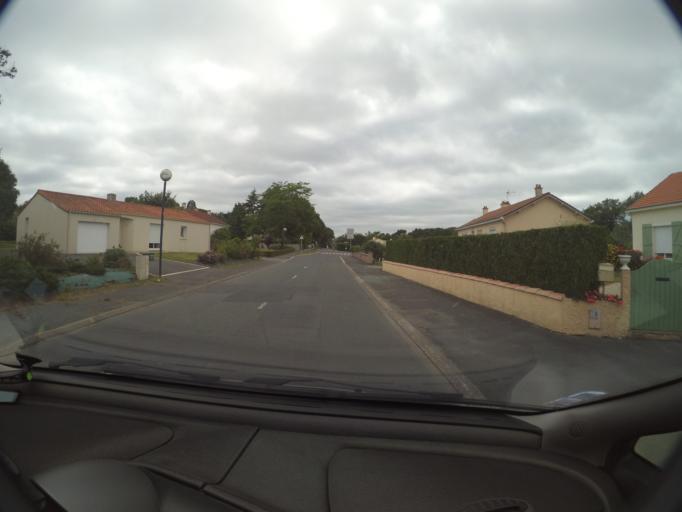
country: FR
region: Pays de la Loire
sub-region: Departement de la Vendee
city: Saint-Hilaire-de-Loulay
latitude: 46.9989
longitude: -1.3352
